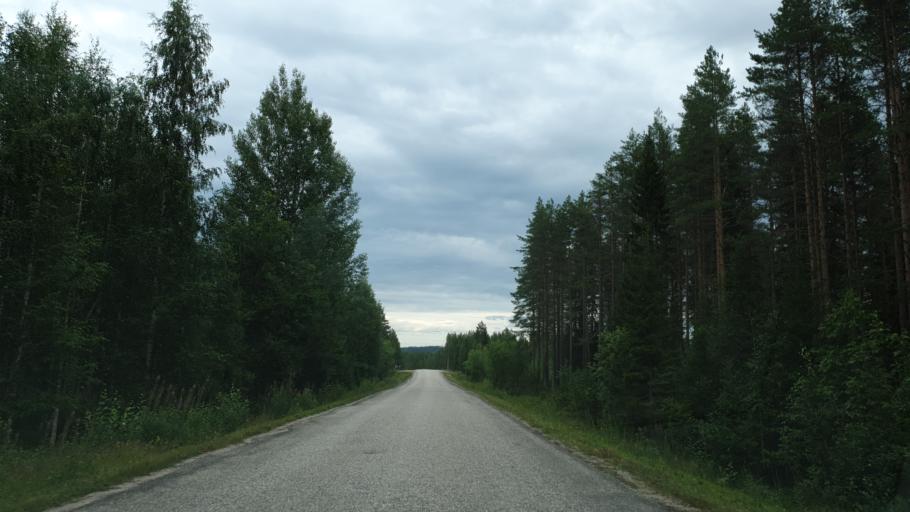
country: FI
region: Kainuu
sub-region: Kehys-Kainuu
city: Kuhmo
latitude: 64.3451
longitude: 29.2758
